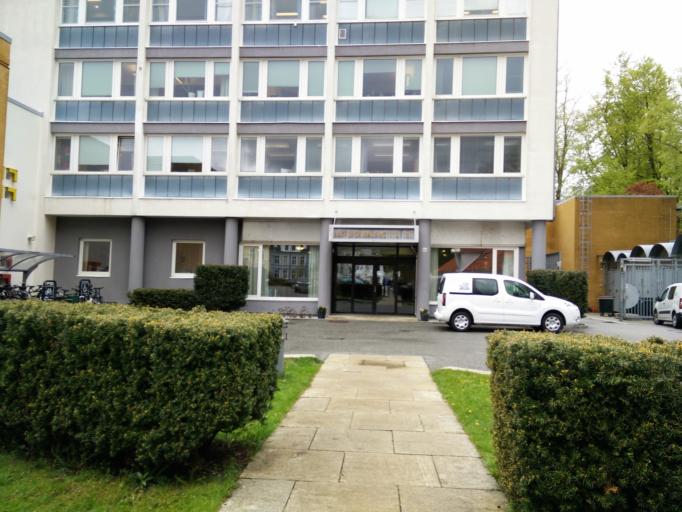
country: NO
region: Hordaland
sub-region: Bergen
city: Bergen
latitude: 60.4001
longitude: 5.3045
